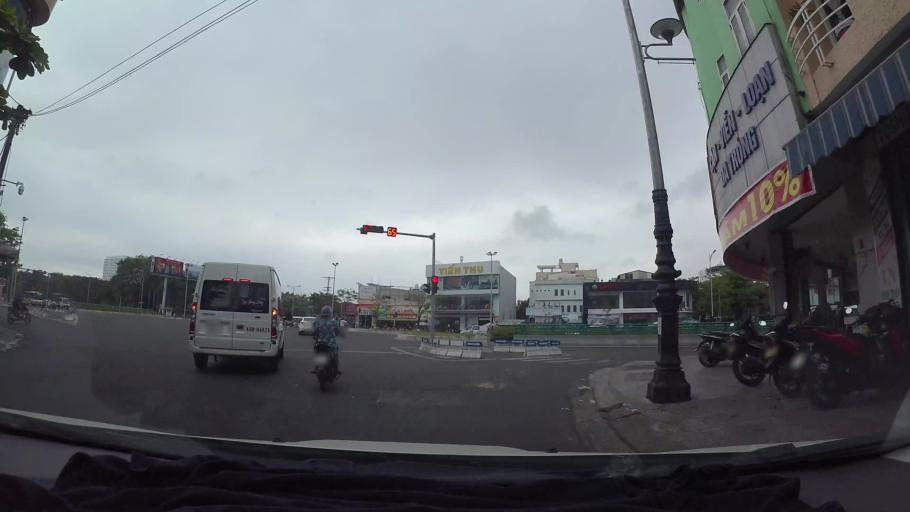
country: VN
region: Da Nang
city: Thanh Khe
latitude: 16.0662
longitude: 108.2019
